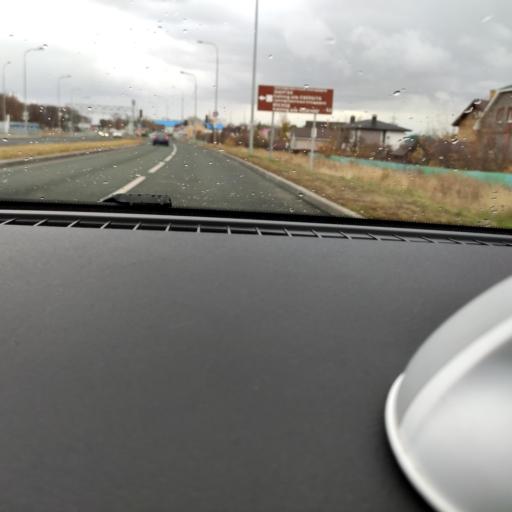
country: RU
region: Samara
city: Samara
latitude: 53.2717
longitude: 50.2331
